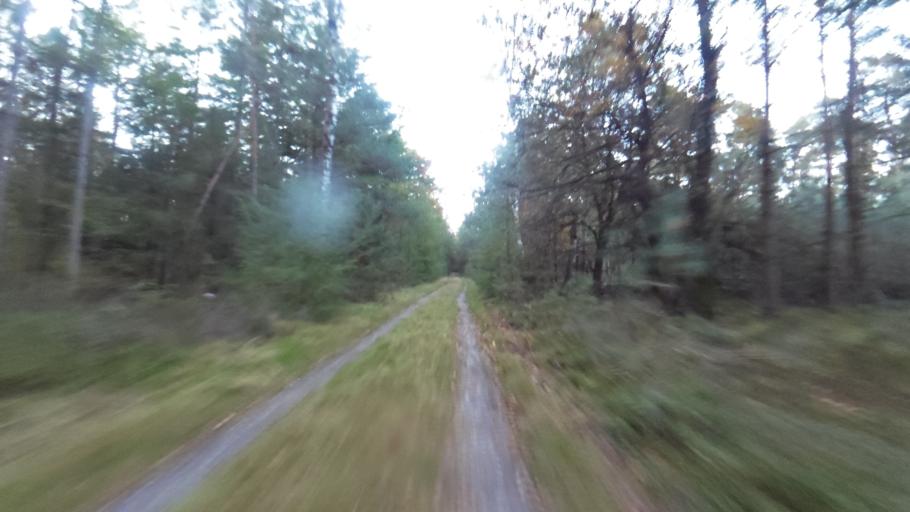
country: NL
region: Gelderland
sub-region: Gemeente Nunspeet
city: Nunspeet
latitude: 52.3356
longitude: 5.7979
